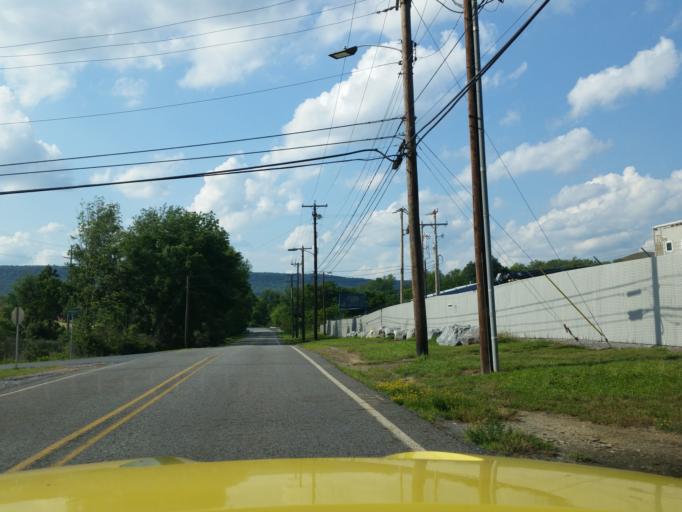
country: US
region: Pennsylvania
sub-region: Lebanon County
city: Jonestown
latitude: 40.4344
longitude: -76.5420
